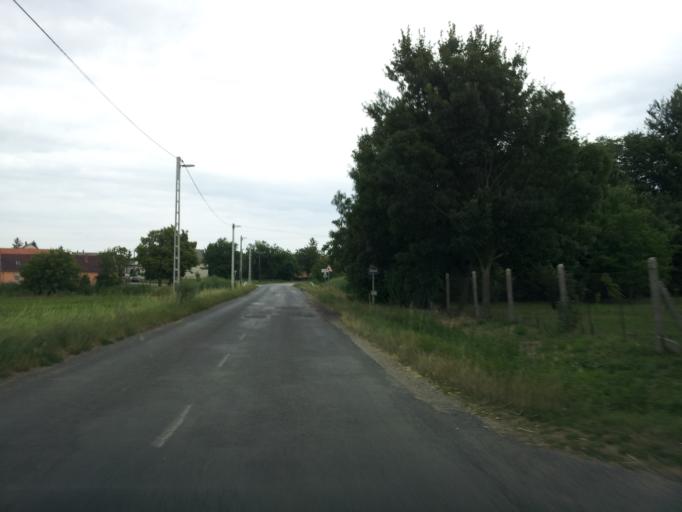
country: HU
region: Veszprem
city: Devecser
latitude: 47.1030
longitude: 17.4259
